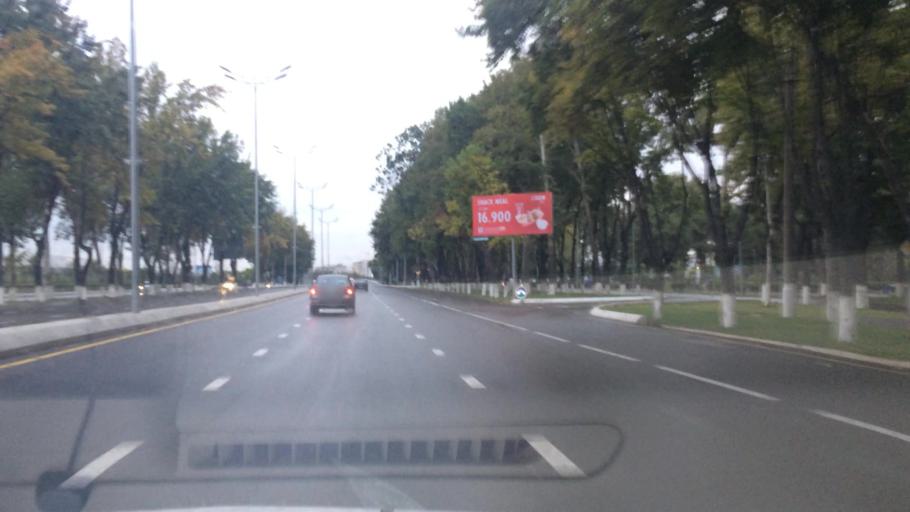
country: UZ
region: Toshkent Shahri
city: Tashkent
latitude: 41.2785
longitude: 69.2082
